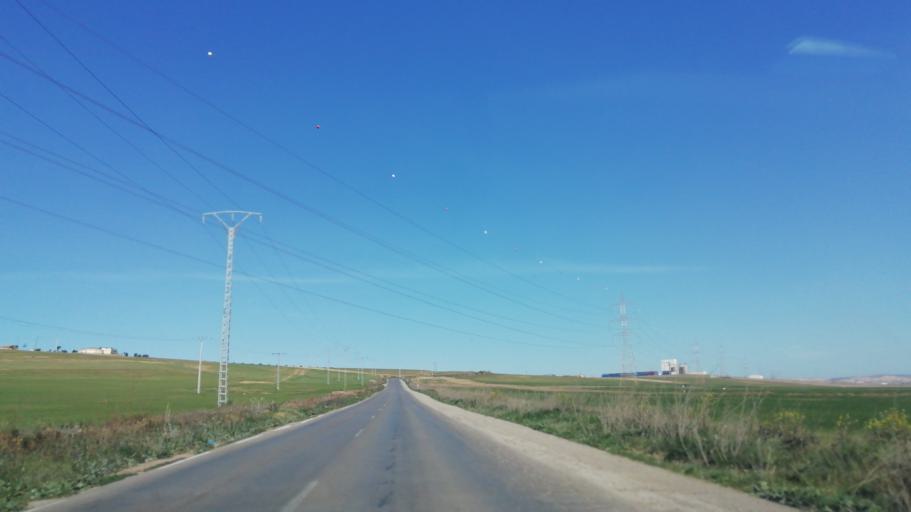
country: DZ
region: Oran
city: Es Senia
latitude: 35.5360
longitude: -0.5850
